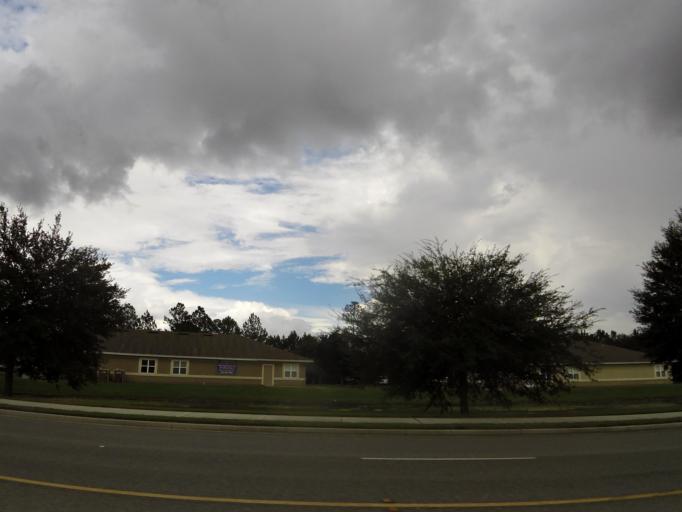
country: US
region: Florida
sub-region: Clay County
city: Asbury Lake
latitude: 30.0511
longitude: -81.8094
